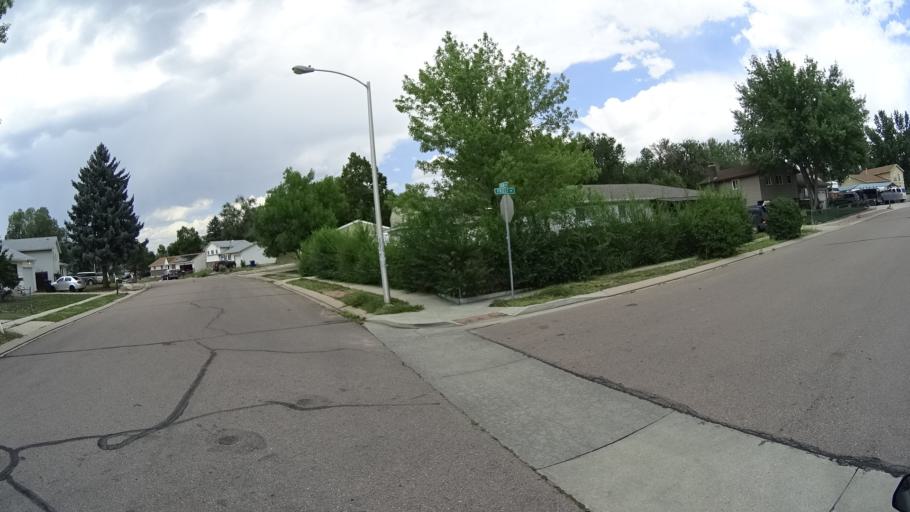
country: US
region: Colorado
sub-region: El Paso County
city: Cimarron Hills
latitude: 38.8296
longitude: -104.7469
